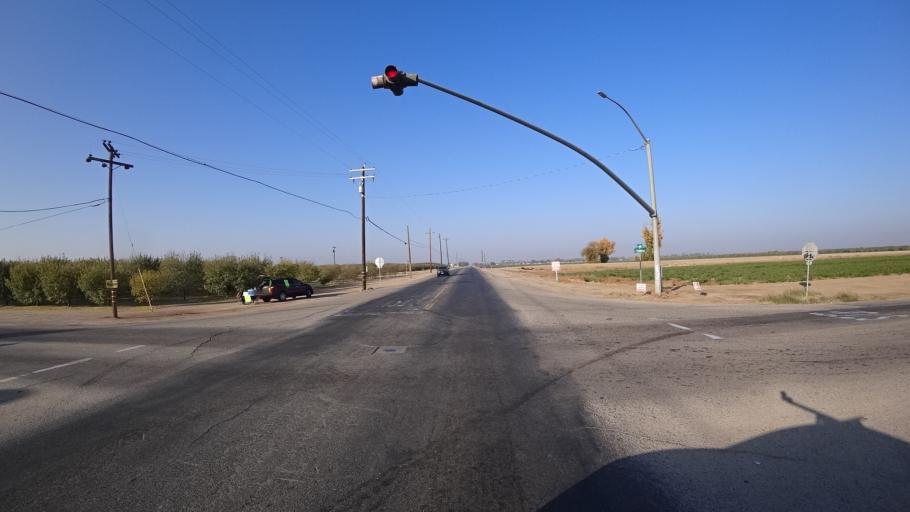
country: US
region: California
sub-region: Kern County
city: Greenfield
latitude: 35.2669
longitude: -118.9853
